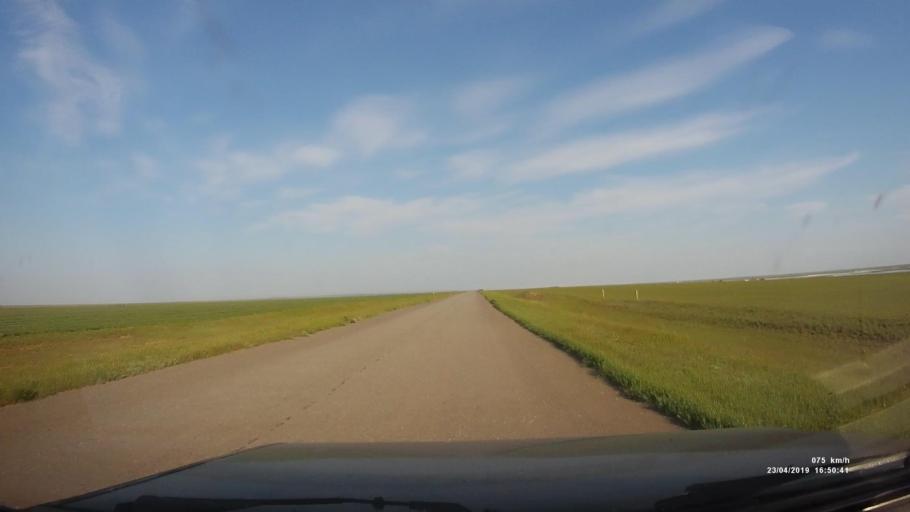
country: RU
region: Kalmykiya
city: Priyutnoye
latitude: 46.3260
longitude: 43.2952
